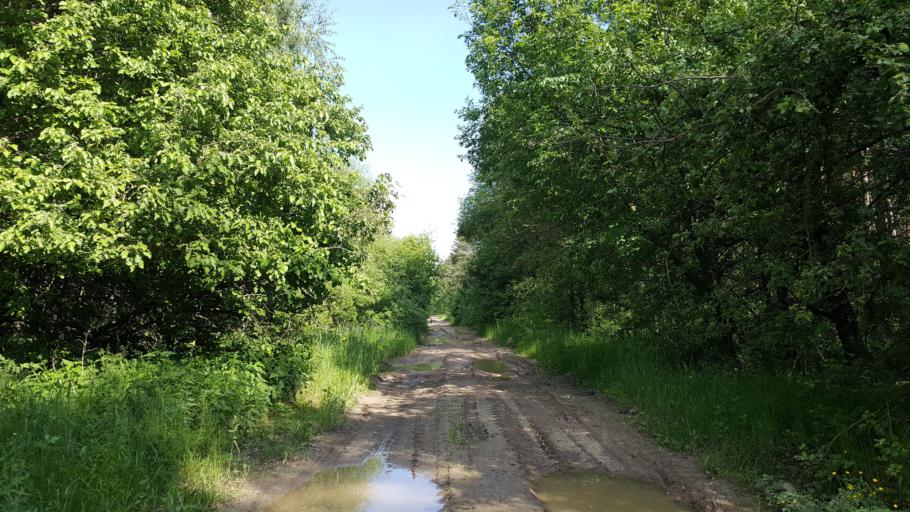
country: BY
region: Brest
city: Kamyanyets
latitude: 52.4259
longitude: 23.6404
